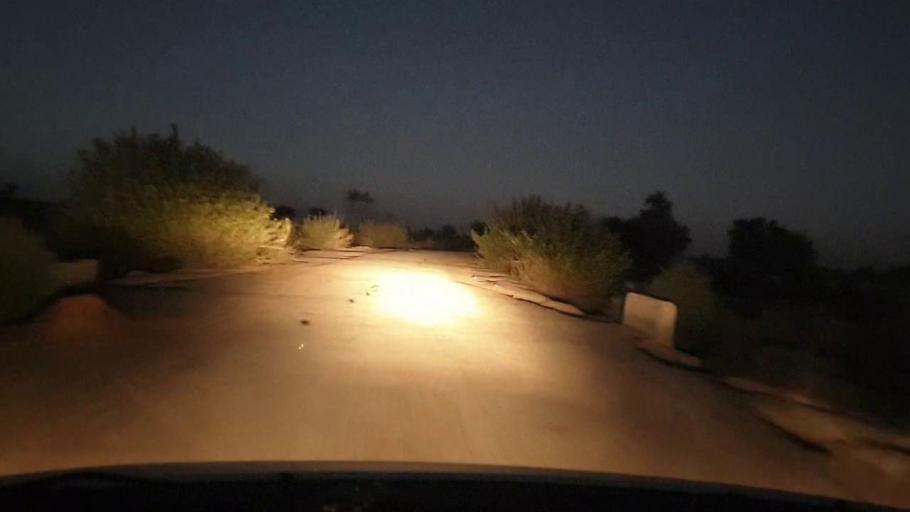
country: PK
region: Sindh
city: Phulji
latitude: 26.9100
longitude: 67.4789
